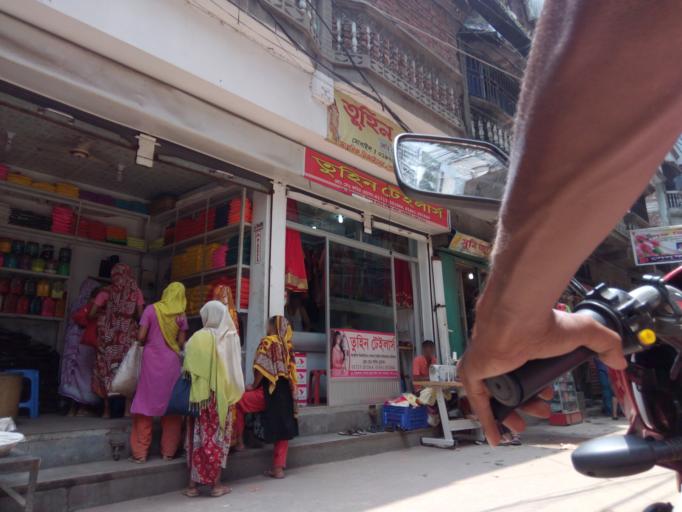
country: BD
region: Dhaka
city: Azimpur
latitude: 23.7138
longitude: 90.3886
